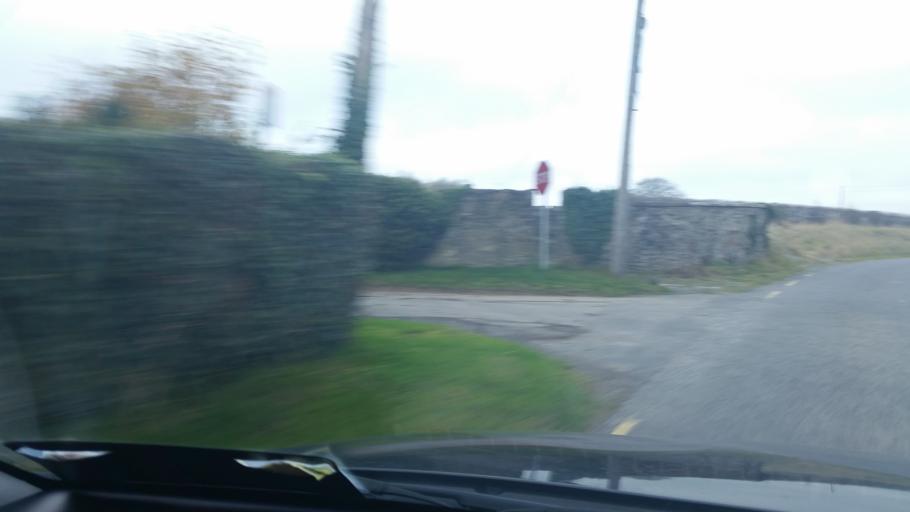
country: IE
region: Leinster
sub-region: Lu
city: Tullyallen
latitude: 53.6987
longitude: -6.4105
